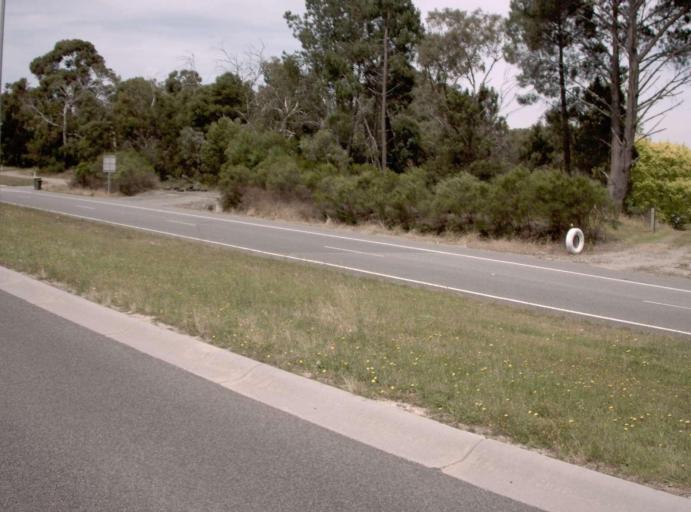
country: AU
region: Victoria
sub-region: Casey
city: Cranbourne South
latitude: -38.1419
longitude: 145.2269
